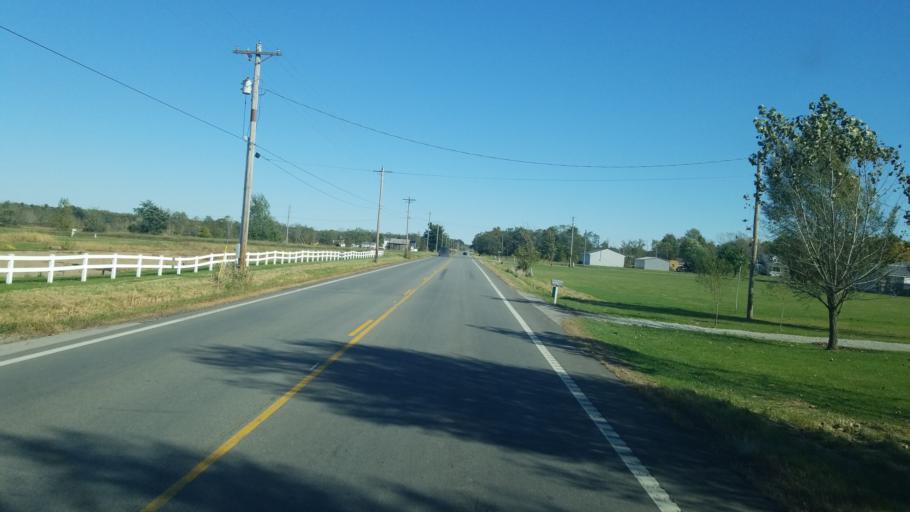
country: US
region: Ohio
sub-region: Huron County
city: New London
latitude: 41.0296
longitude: -82.3473
